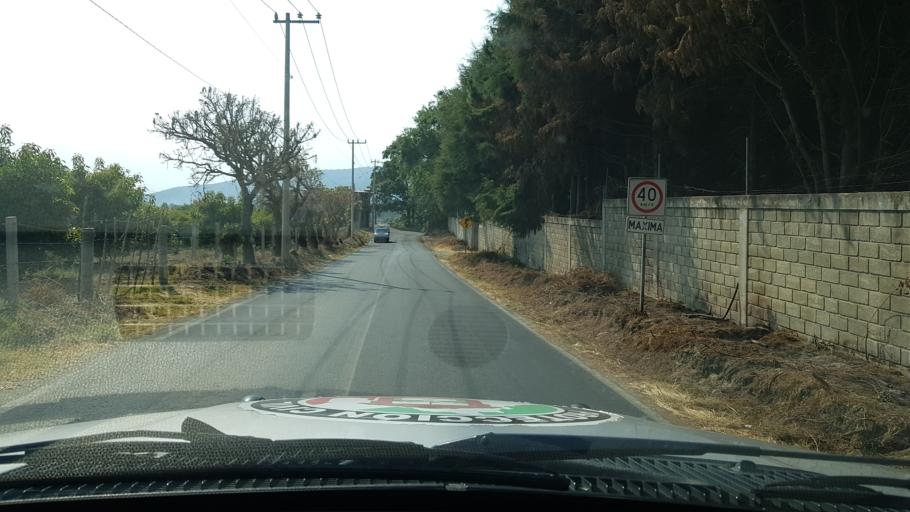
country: MX
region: Mexico
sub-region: Ozumba
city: San Jose Tlacotitlan
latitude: 18.9869
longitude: -98.8172
